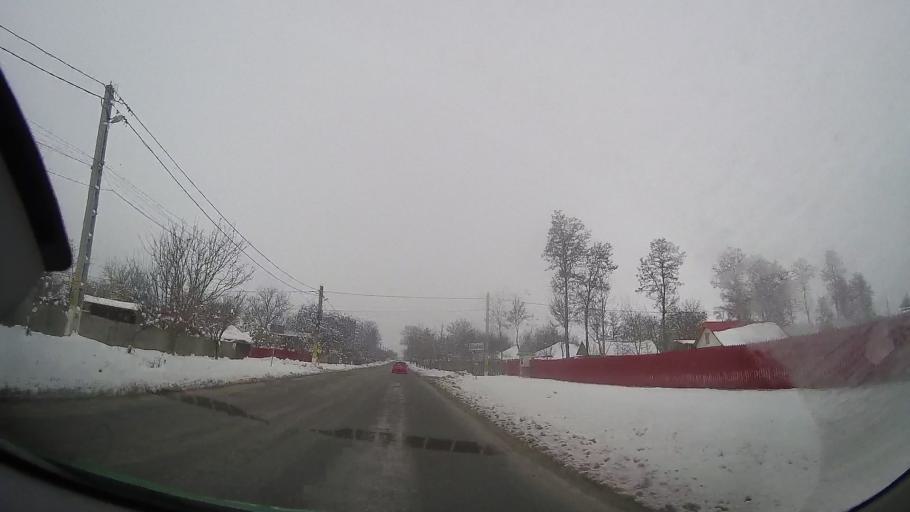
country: RO
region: Vaslui
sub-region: Comuna Negresti
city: Negresti
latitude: 46.8392
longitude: 27.4186
